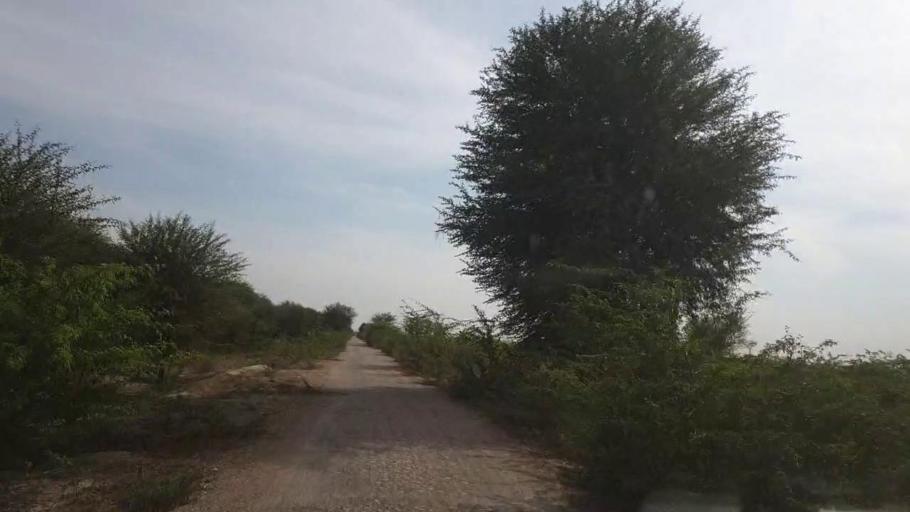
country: PK
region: Sindh
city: Nabisar
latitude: 25.0202
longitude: 69.5623
